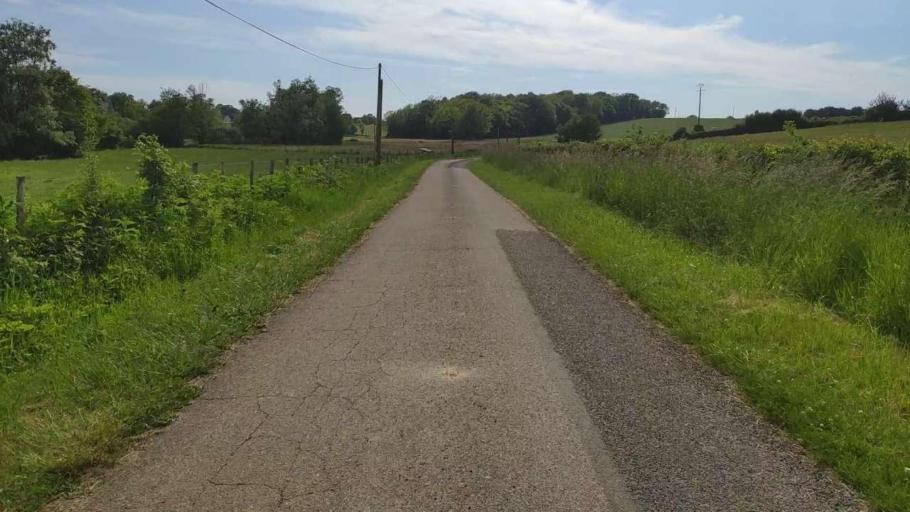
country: FR
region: Bourgogne
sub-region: Departement de Saone-et-Loire
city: Saint-Germain-du-Bois
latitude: 46.8115
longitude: 5.3489
